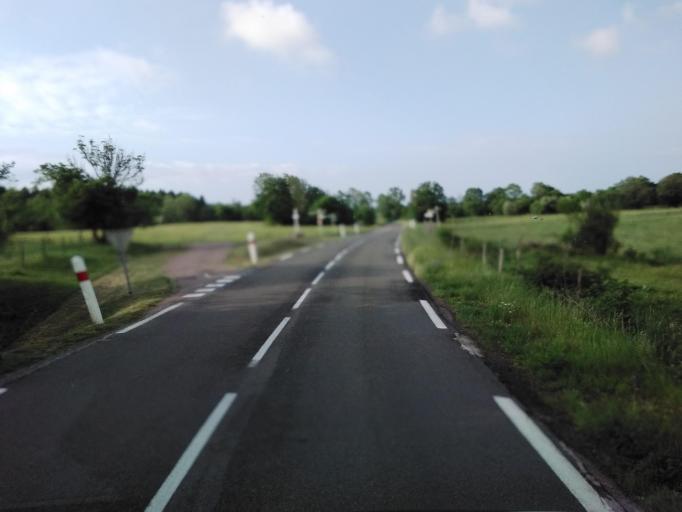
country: FR
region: Franche-Comte
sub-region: Departement du Jura
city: Arbois
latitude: 46.8266
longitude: 5.8219
